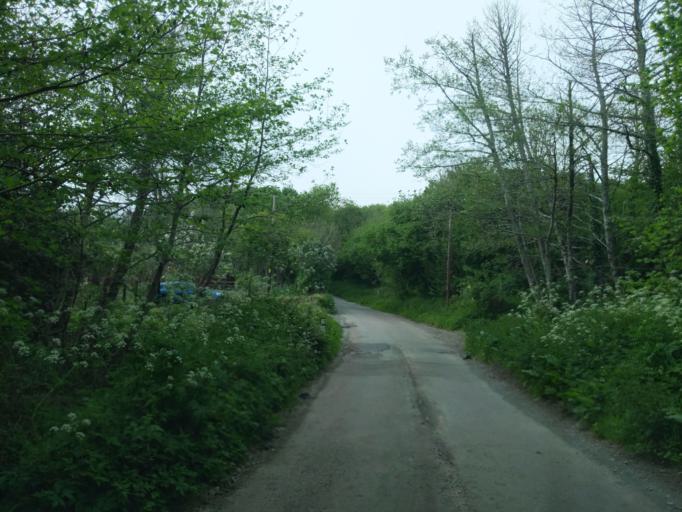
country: GB
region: England
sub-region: Devon
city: Plympton
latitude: 50.4324
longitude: -4.0588
